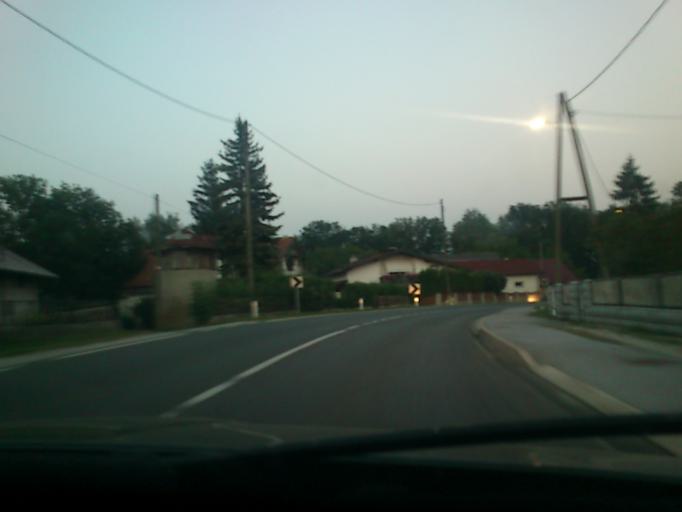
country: SI
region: Duplek
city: Spodnji Duplek
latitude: 46.4887
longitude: 15.7294
